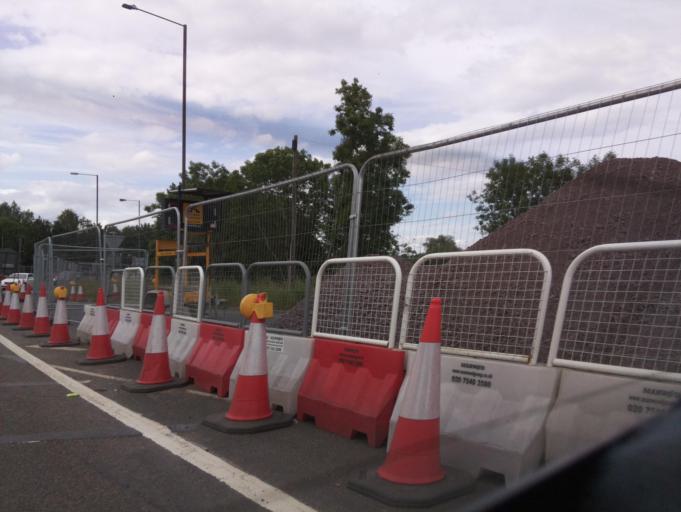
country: GB
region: England
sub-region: Worcestershire
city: Worcester
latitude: 52.1680
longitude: -2.2417
